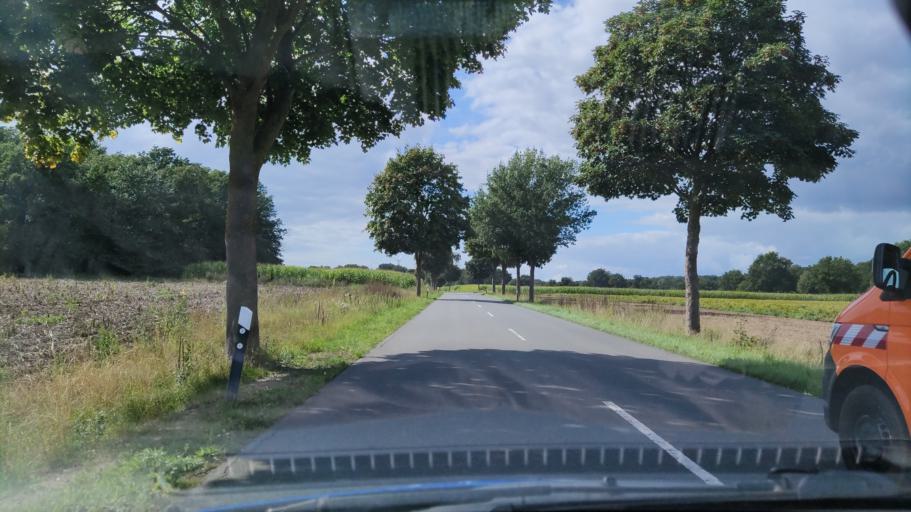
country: DE
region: Lower Saxony
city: Oetzen
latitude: 53.0212
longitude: 10.6580
